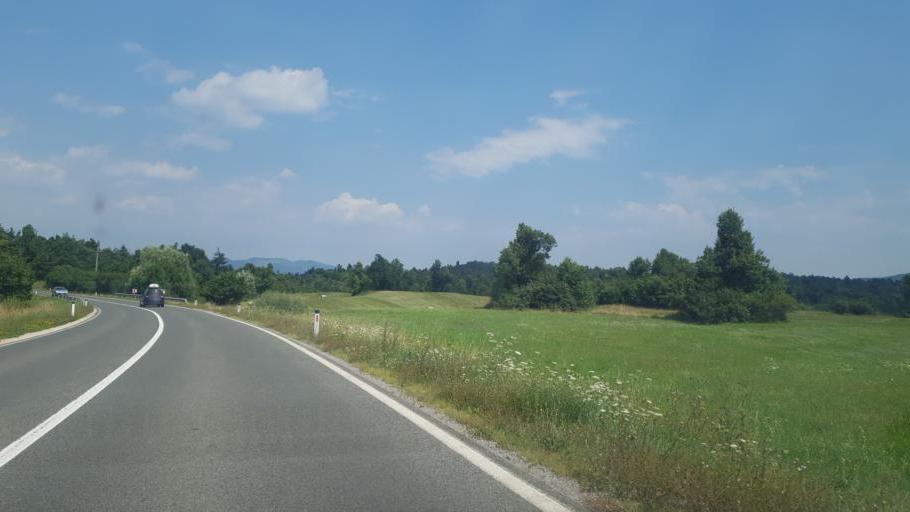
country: SI
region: Pivka
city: Pivka
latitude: 45.7218
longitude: 14.1916
